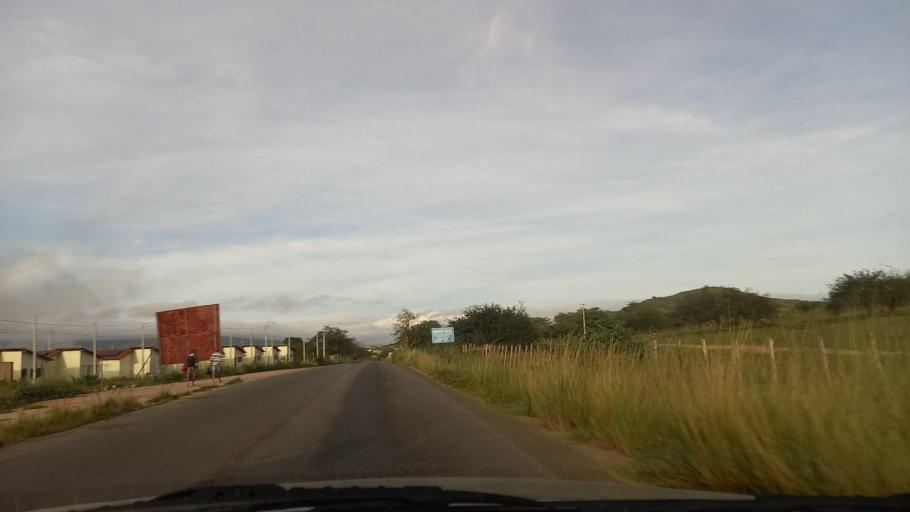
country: BR
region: Pernambuco
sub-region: Bezerros
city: Bezerros
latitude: -8.2153
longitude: -35.7439
